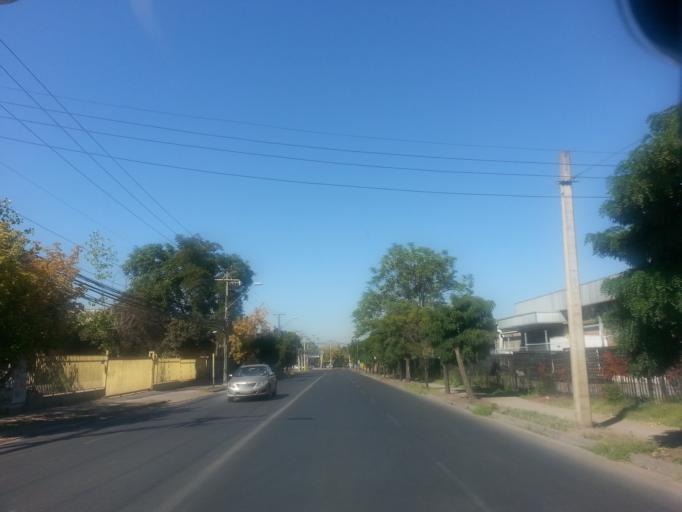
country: CL
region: Santiago Metropolitan
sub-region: Provincia de Santiago
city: Villa Presidente Frei, Nunoa, Santiago, Chile
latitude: -33.4565
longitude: -70.5451
